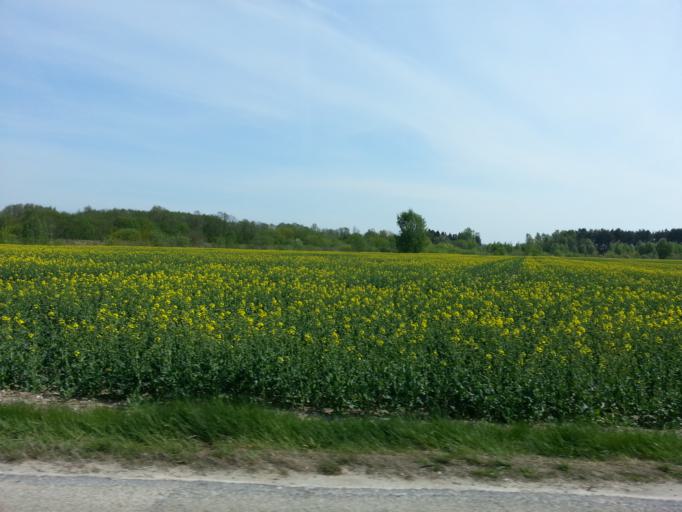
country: LT
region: Panevezys
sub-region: Panevezys City
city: Panevezys
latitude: 55.8059
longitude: 24.2728
